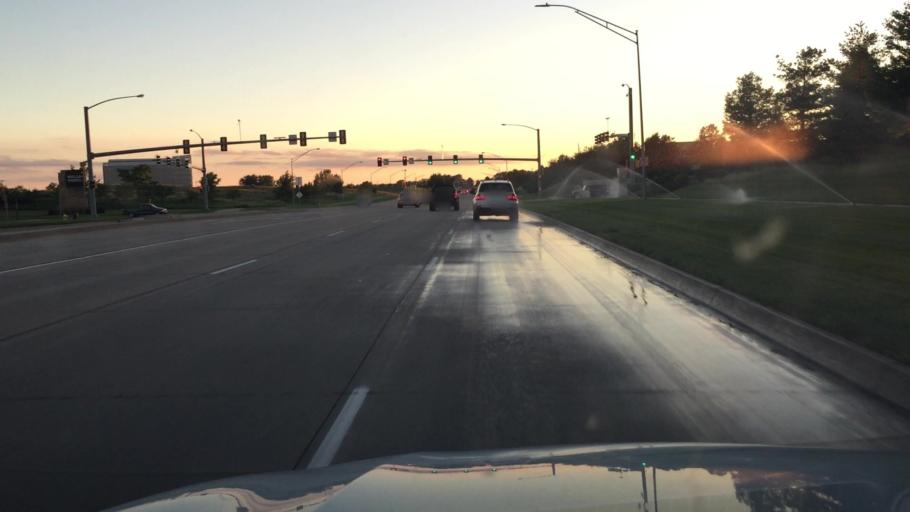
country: US
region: Iowa
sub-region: Polk County
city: Clive
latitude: 41.5617
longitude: -93.8024
